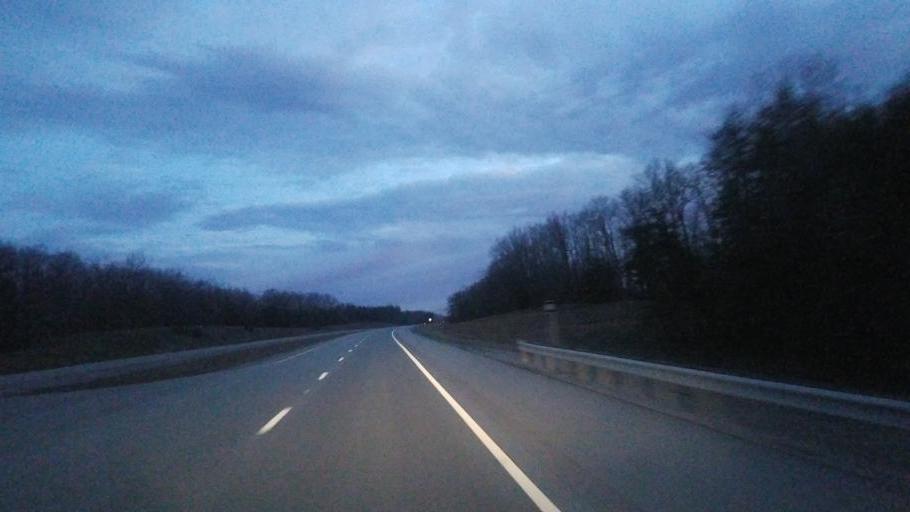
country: US
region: Tennessee
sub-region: Van Buren County
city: Spencer
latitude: 35.5797
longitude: -85.4715
